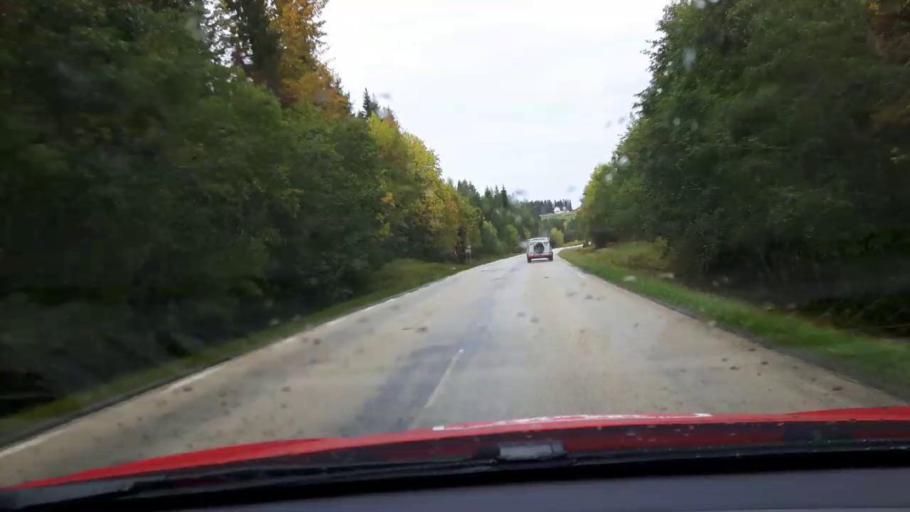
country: SE
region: Jaemtland
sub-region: Bergs Kommun
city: Hoverberg
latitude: 62.9520
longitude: 14.3389
